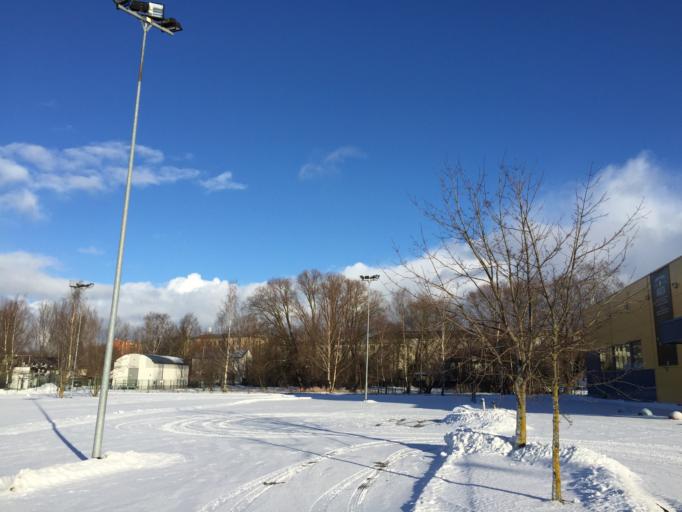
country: LV
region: Riga
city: Riga
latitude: 56.9301
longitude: 24.1576
